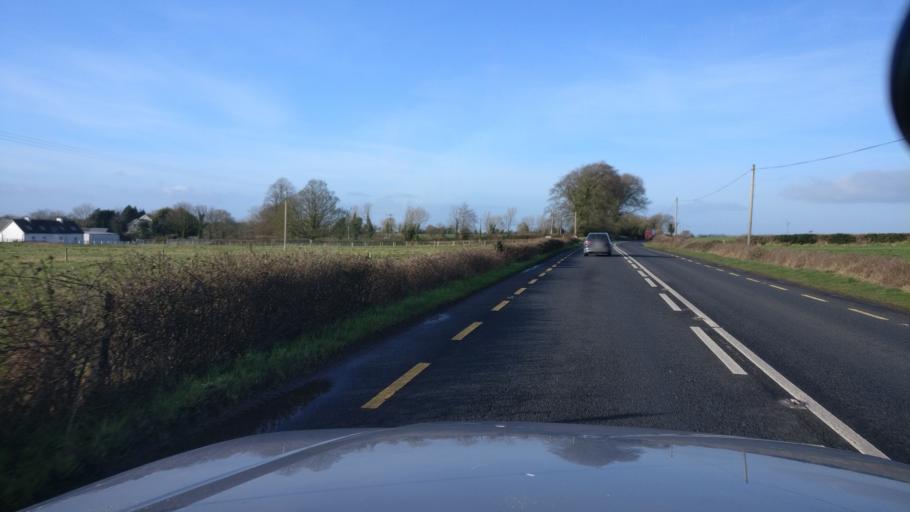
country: IE
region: Leinster
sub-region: Uibh Fhaili
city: Tullamore
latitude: 53.2012
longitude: -7.4319
